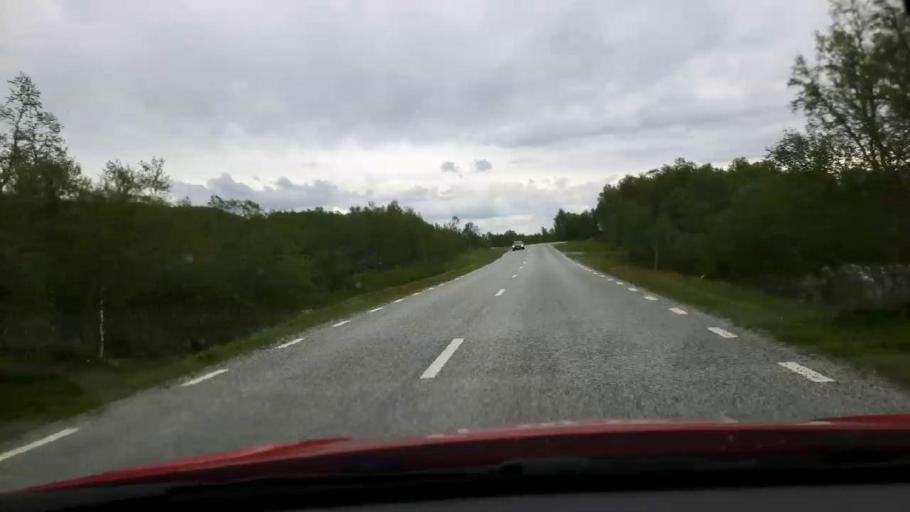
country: NO
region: Sor-Trondelag
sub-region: Tydal
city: Aas
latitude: 62.6113
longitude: 12.1526
